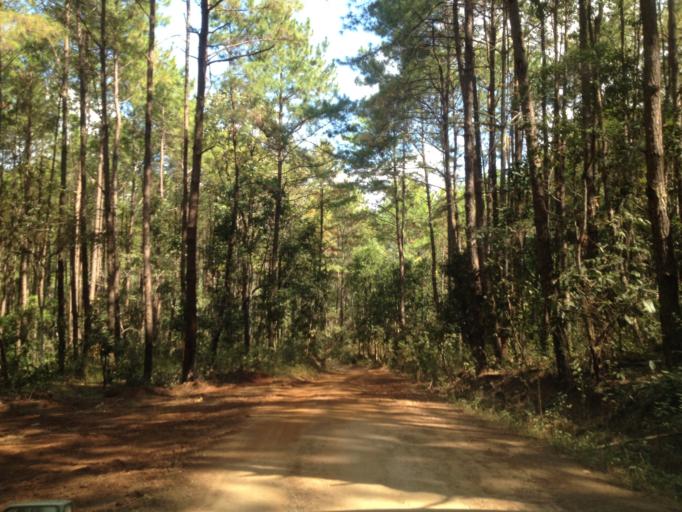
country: TH
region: Mae Hong Son
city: Ban Huai I Huak
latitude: 18.1068
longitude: 98.1758
